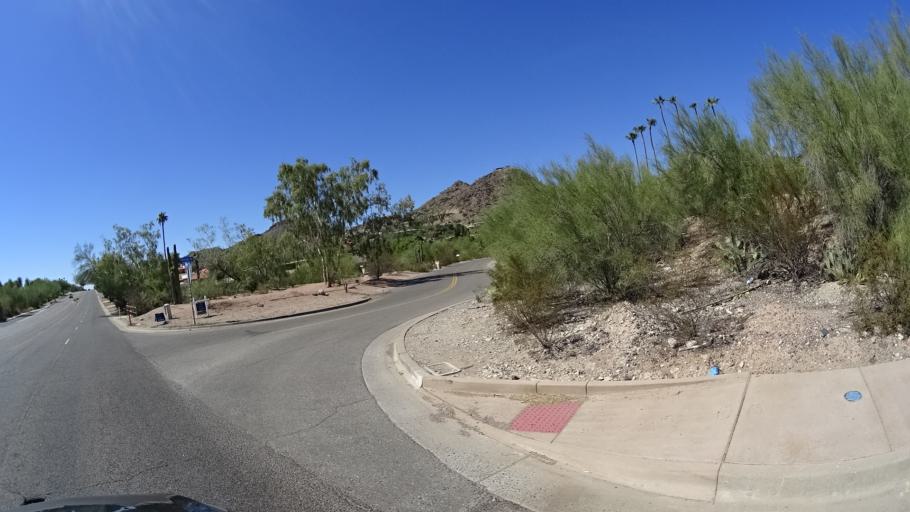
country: US
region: Arizona
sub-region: Maricopa County
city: Paradise Valley
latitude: 33.5314
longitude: -111.9850
